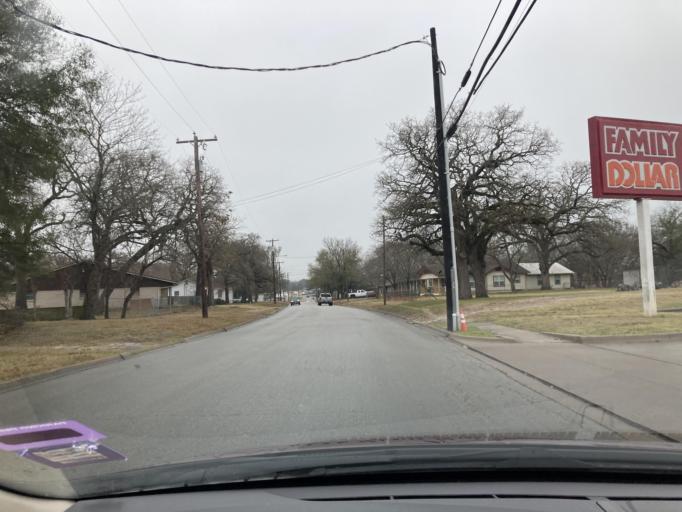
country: US
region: Texas
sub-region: Navarro County
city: Corsicana
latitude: 32.1044
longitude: -96.4734
